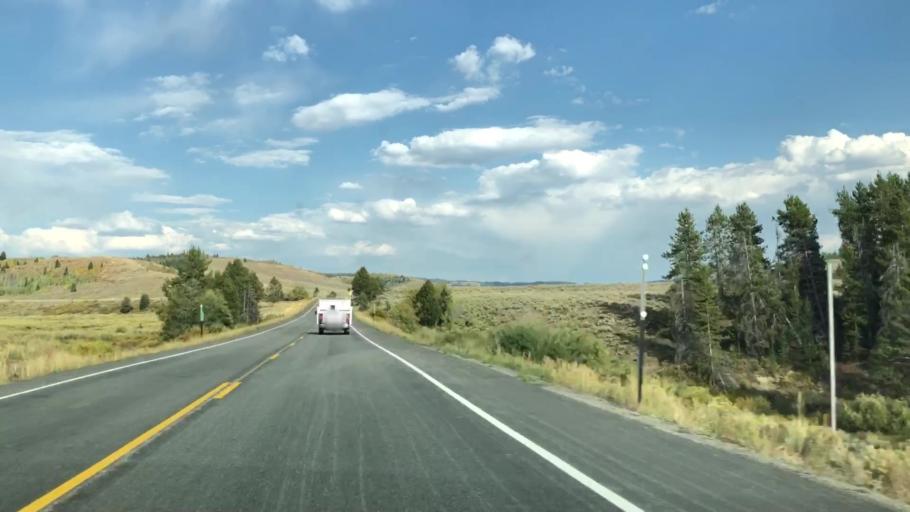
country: US
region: Wyoming
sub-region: Teton County
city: Hoback
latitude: 43.1549
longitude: -110.3109
